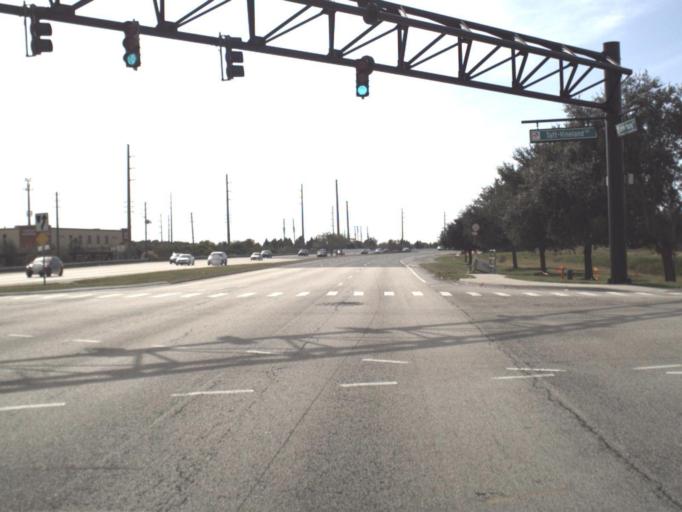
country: US
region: Florida
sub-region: Orange County
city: Williamsburg
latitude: 28.4166
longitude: -81.4230
